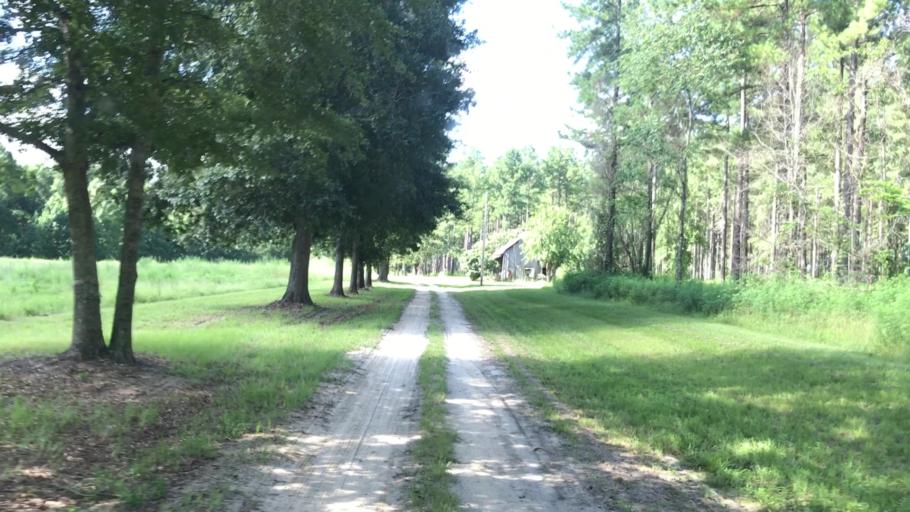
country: US
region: Georgia
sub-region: Jefferson County
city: Wadley
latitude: 32.8142
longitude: -82.3337
